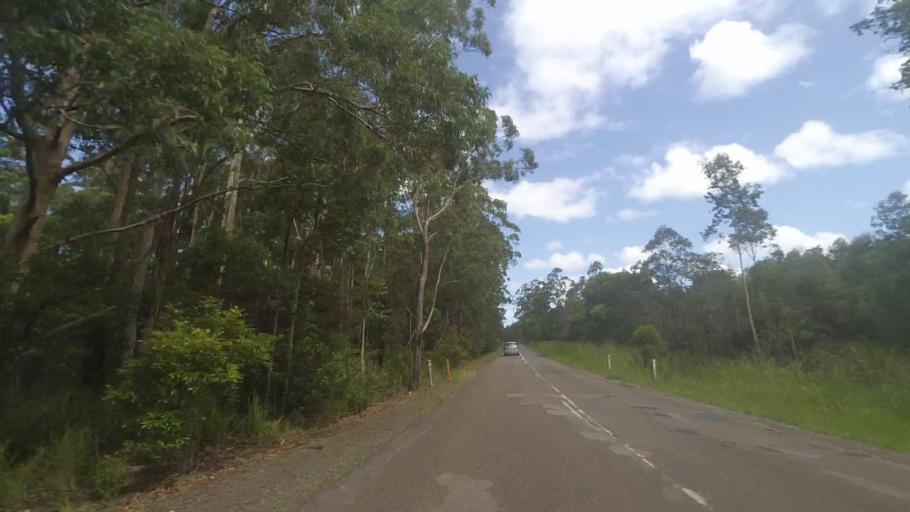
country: AU
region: New South Wales
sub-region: Great Lakes
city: Bulahdelah
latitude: -32.3935
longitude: 152.2523
